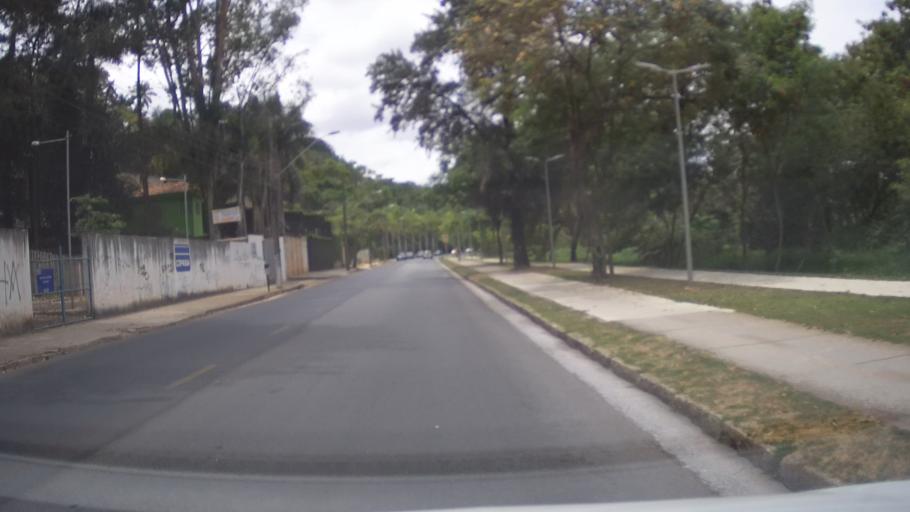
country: BR
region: Minas Gerais
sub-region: Belo Horizonte
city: Belo Horizonte
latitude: -19.8504
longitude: -44.0018
